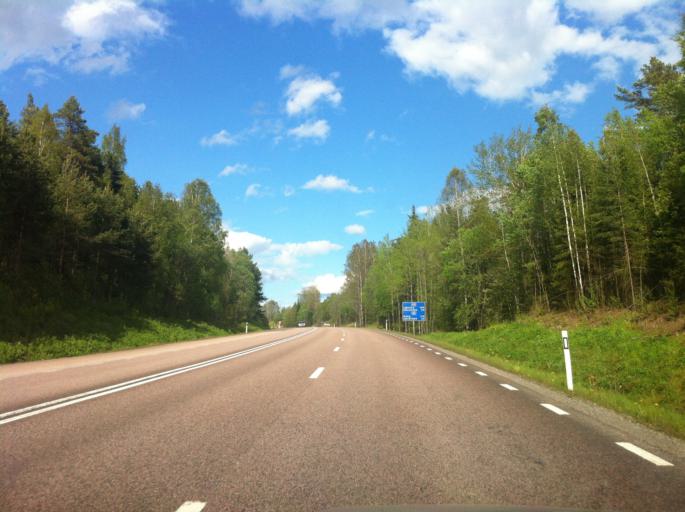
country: SE
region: Vaermland
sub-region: Filipstads Kommun
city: Filipstad
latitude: 59.7132
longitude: 14.1752
